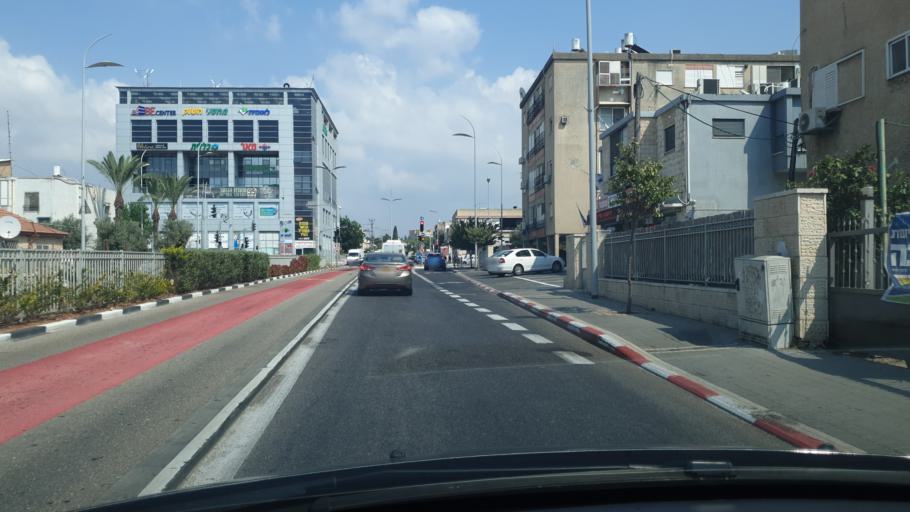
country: IL
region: Haifa
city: Qiryat Ata
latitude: 32.8125
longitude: 35.1038
